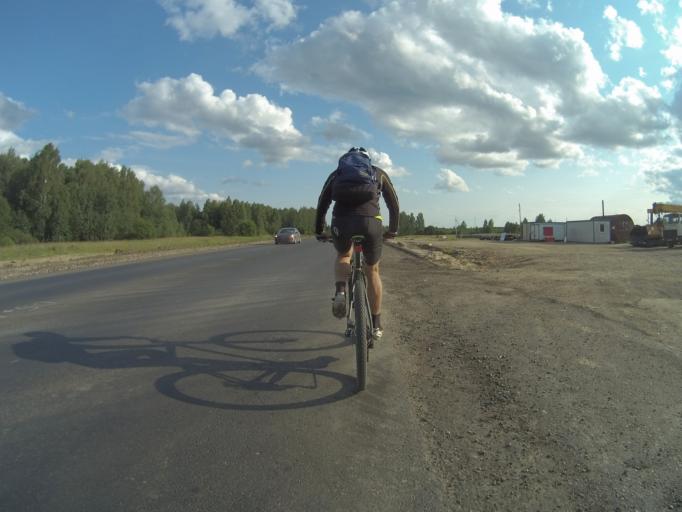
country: RU
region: Vladimir
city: Kideksha
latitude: 56.5269
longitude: 40.5572
